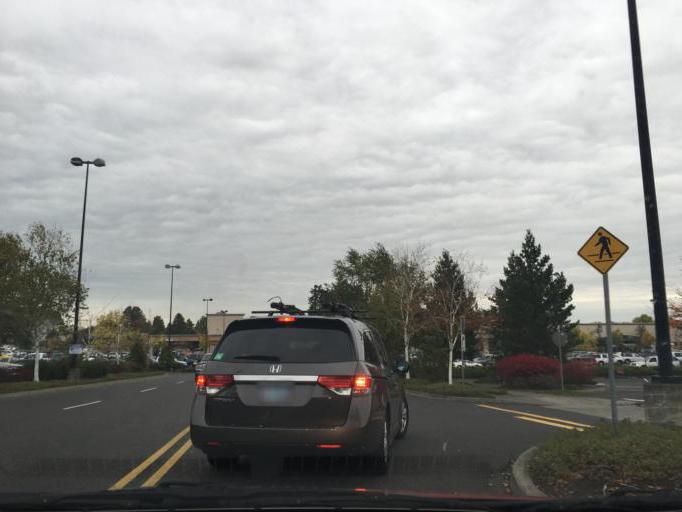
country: US
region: Oregon
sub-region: Multnomah County
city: Lents
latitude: 45.5171
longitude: -122.5623
